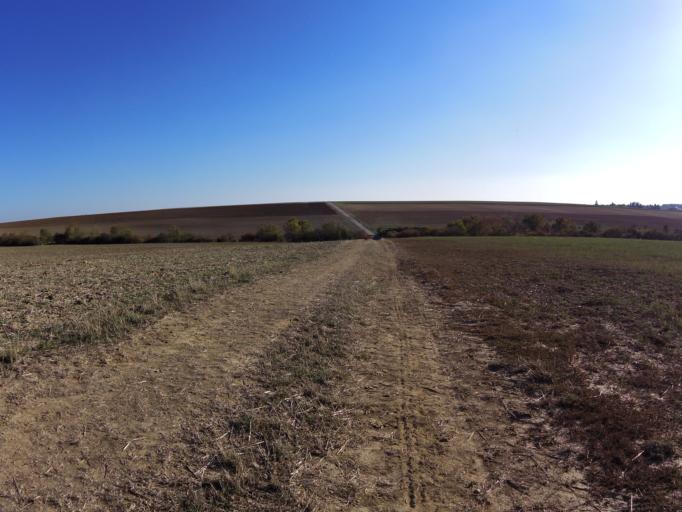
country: DE
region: Bavaria
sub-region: Regierungsbezirk Unterfranken
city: Eibelstadt
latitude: 49.7076
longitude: 9.9766
